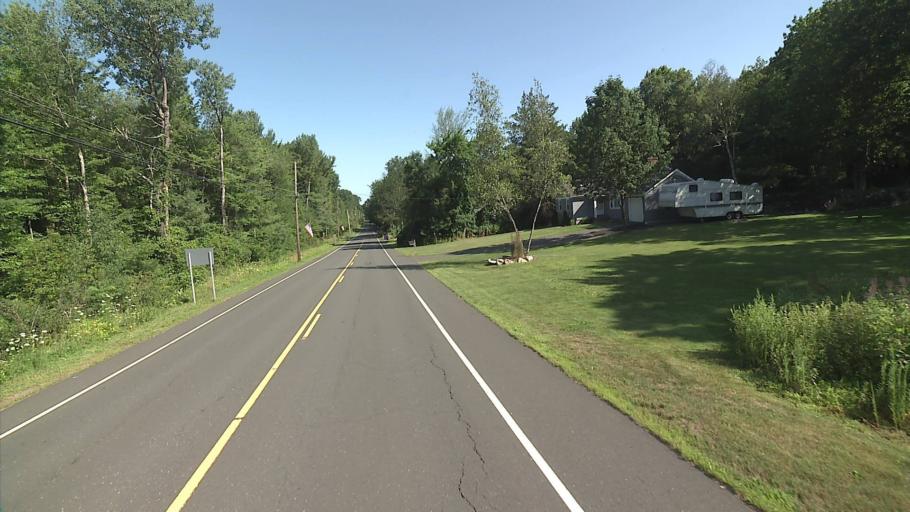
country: US
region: Connecticut
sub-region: Hartford County
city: North Granby
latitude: 42.0010
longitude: -72.9075
